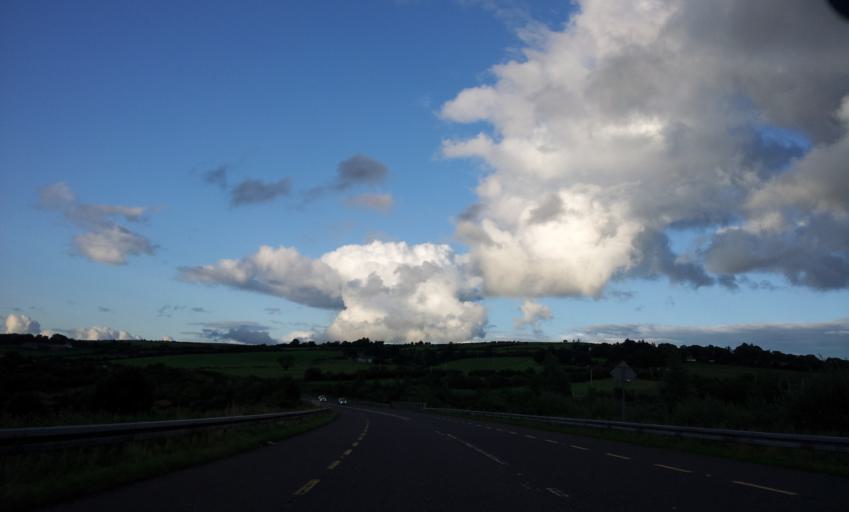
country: IE
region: Munster
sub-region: County Limerick
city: Abbeyfeale
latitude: 52.3119
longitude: -9.3643
